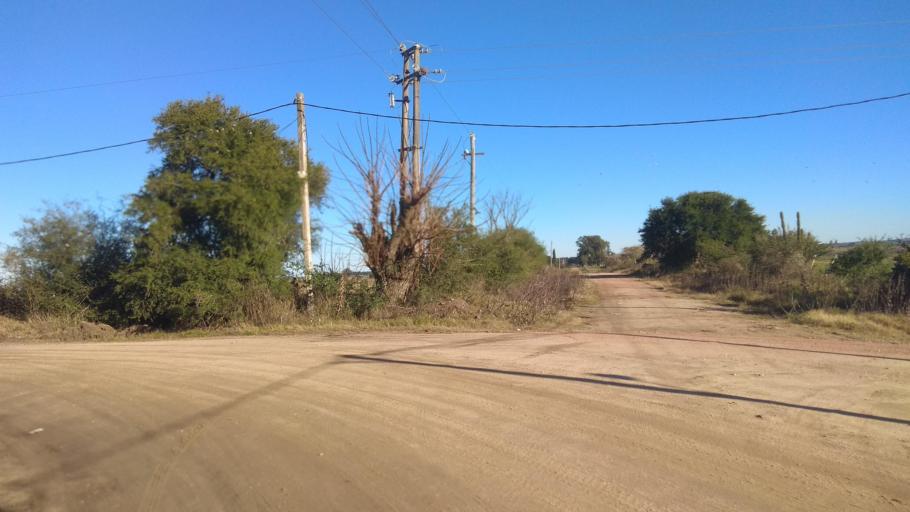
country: UY
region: Florida
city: Florida
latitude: -34.0921
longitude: -56.2511
